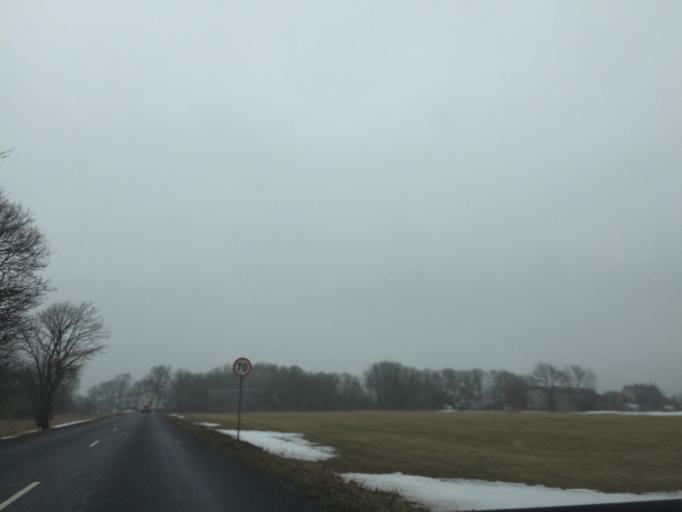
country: EE
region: Saare
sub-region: Kuressaare linn
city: Kuressaare
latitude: 58.3013
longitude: 22.8148
